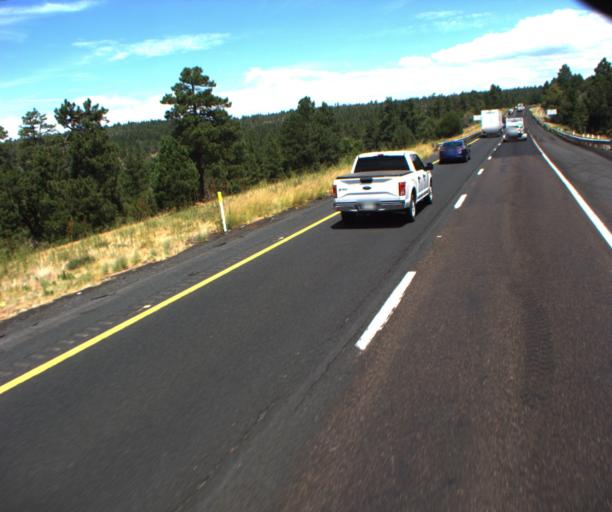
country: US
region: Arizona
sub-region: Yavapai County
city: Village of Oak Creek (Big Park)
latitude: 34.8157
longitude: -111.6112
